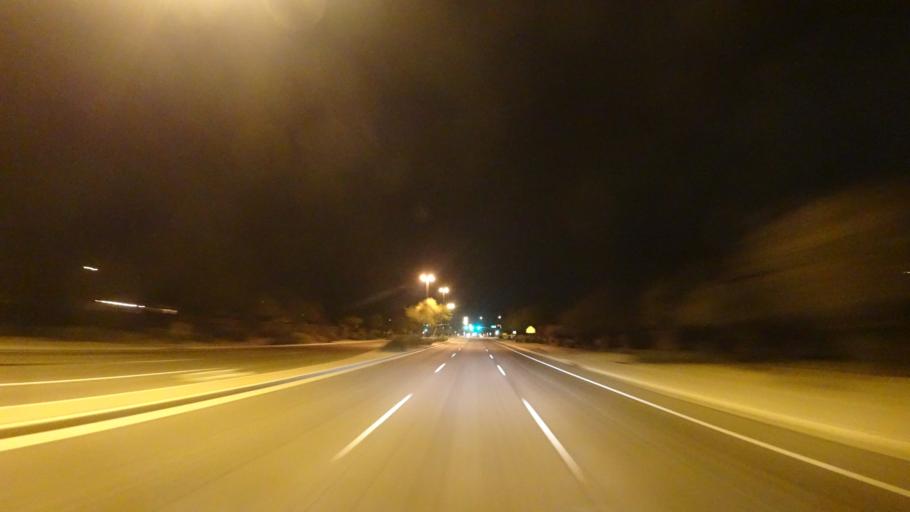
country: US
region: Arizona
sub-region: Maricopa County
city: Gilbert
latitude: 33.3021
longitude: -111.7211
